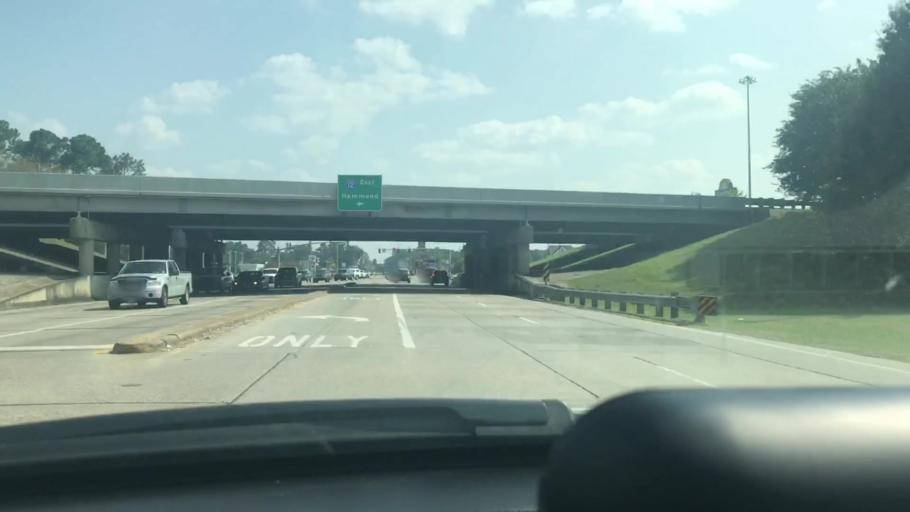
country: US
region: Louisiana
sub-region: Livingston Parish
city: Denham Springs
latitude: 30.4557
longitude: -90.9566
